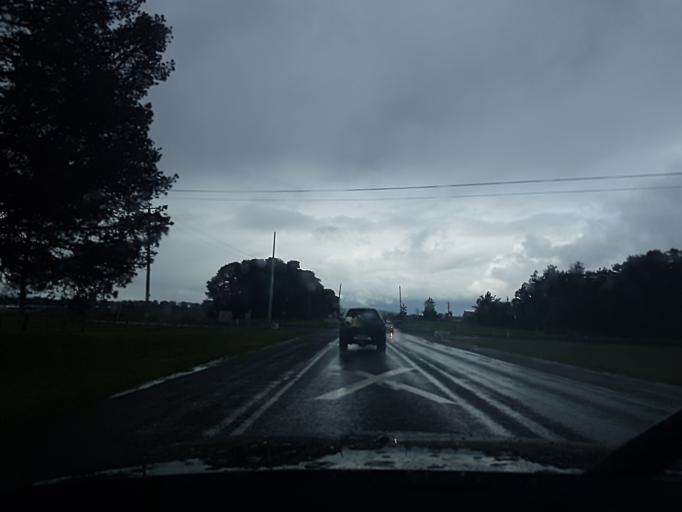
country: AU
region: Victoria
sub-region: Ballarat North
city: Newington
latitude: -37.5345
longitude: 143.8026
